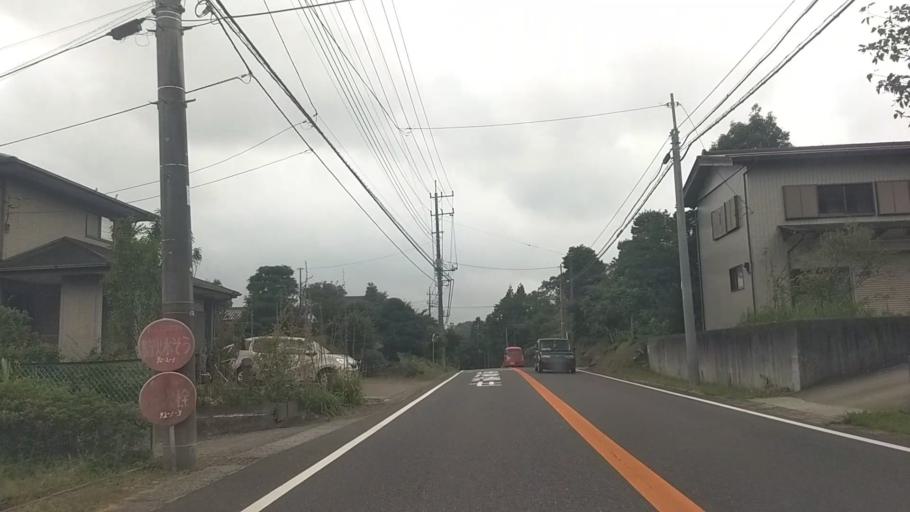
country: JP
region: Chiba
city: Kawaguchi
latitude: 35.2266
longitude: 140.0745
